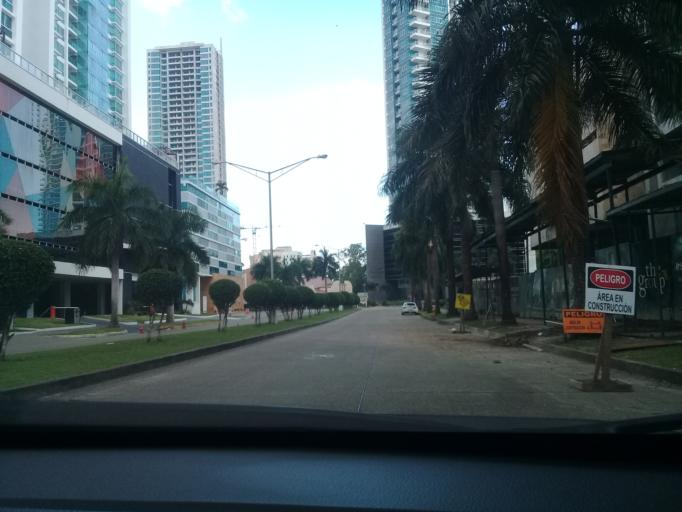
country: PA
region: Panama
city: San Miguelito
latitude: 9.0109
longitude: -79.4714
